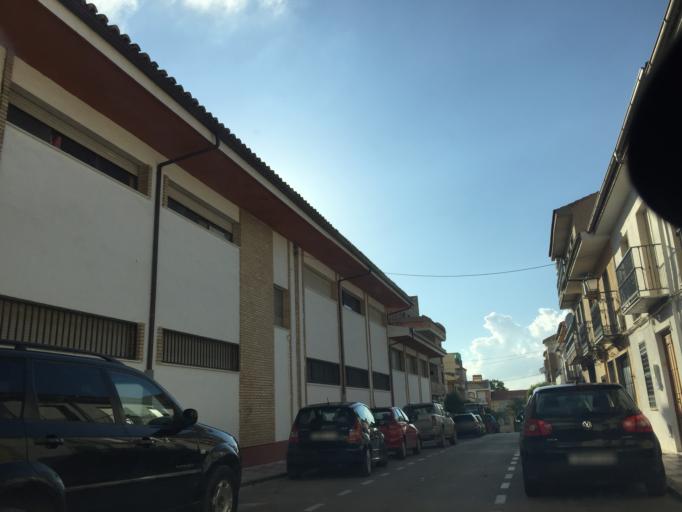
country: ES
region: Andalusia
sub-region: Provincia de Jaen
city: Mancha Real
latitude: 37.7829
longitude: -3.6095
